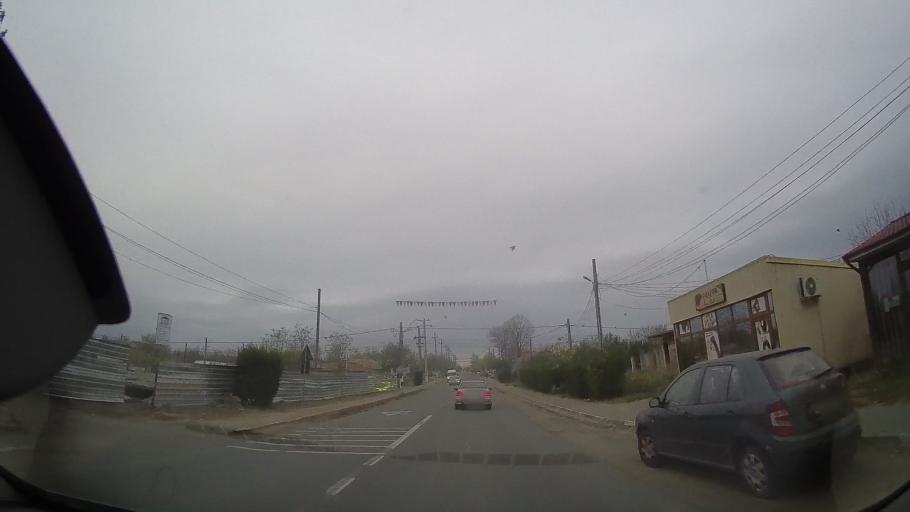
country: RO
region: Ialomita
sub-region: Oras Amara
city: Amara
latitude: 44.6214
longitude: 27.3130
